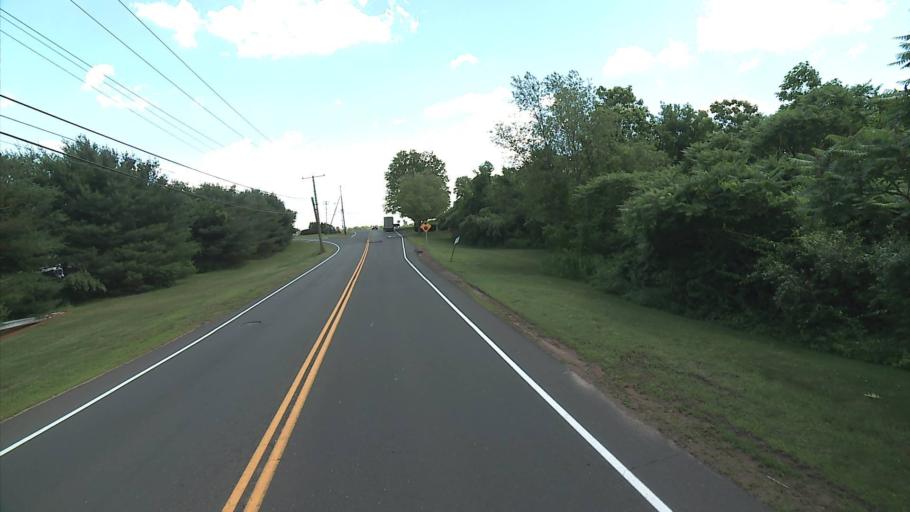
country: US
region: Connecticut
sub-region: Hartford County
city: Hazardville
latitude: 42.0144
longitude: -72.5156
